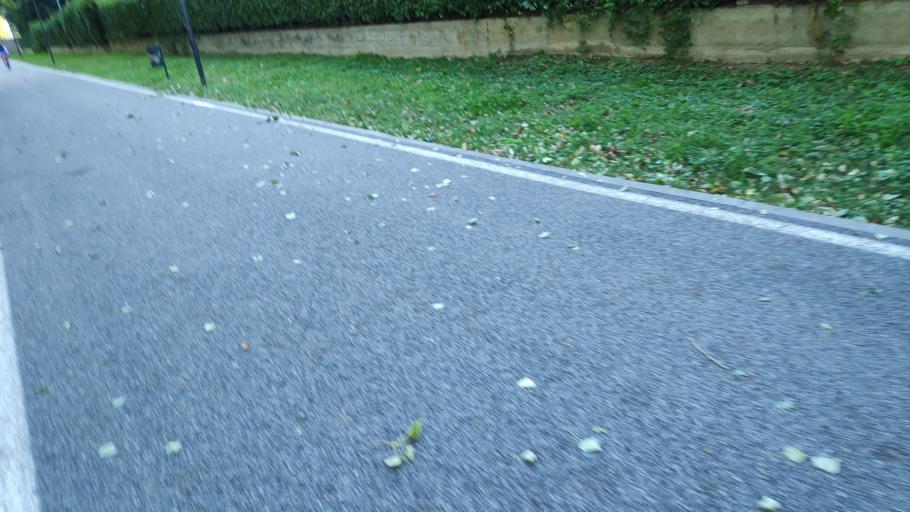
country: IT
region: Lombardy
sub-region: Citta metropolitana di Milano
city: Melzo
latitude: 45.5003
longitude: 9.4331
